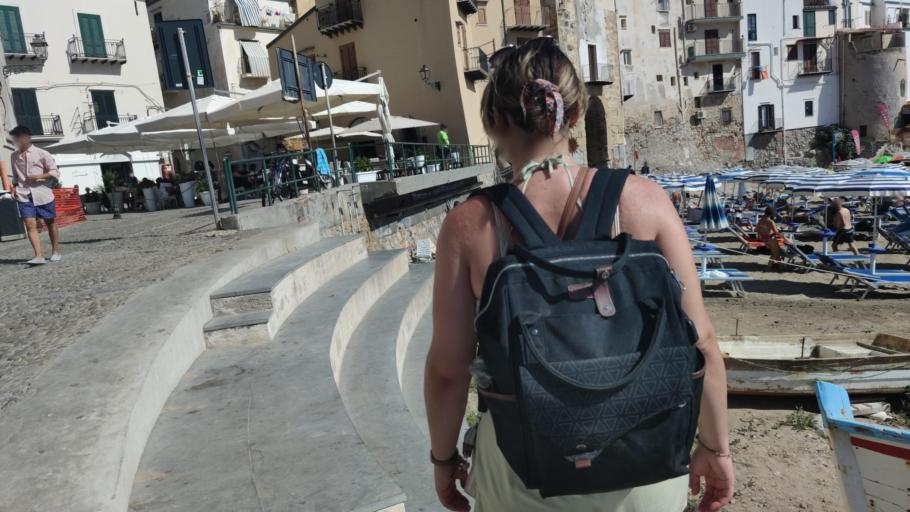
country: IT
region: Sicily
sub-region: Palermo
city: Cefalu
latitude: 38.0403
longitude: 14.0196
